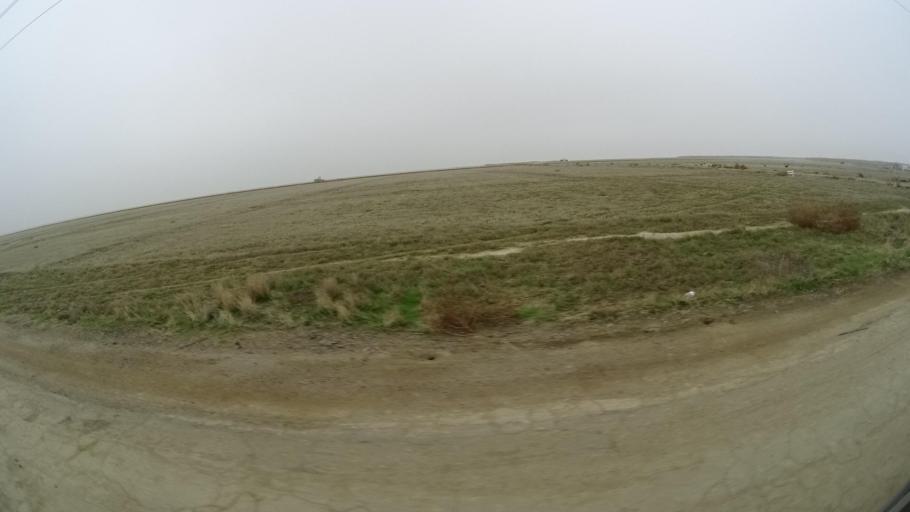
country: US
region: California
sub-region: Tulare County
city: Alpaugh
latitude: 35.7897
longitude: -119.4011
